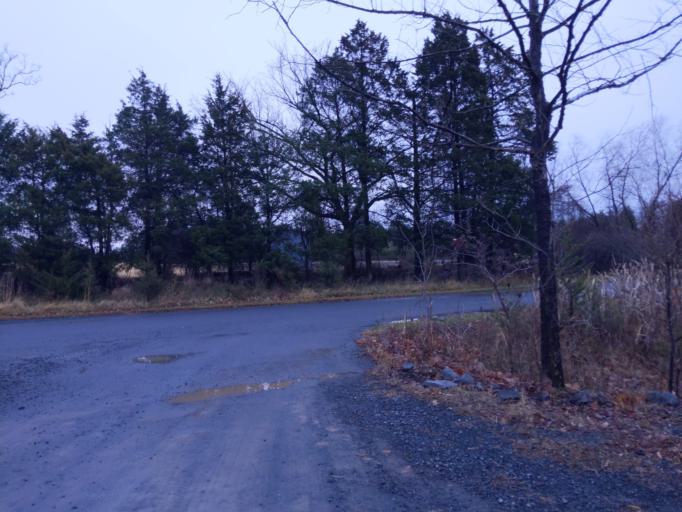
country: US
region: Virginia
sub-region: Loudoun County
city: Dulles Town Center
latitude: 39.0157
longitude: -77.4038
